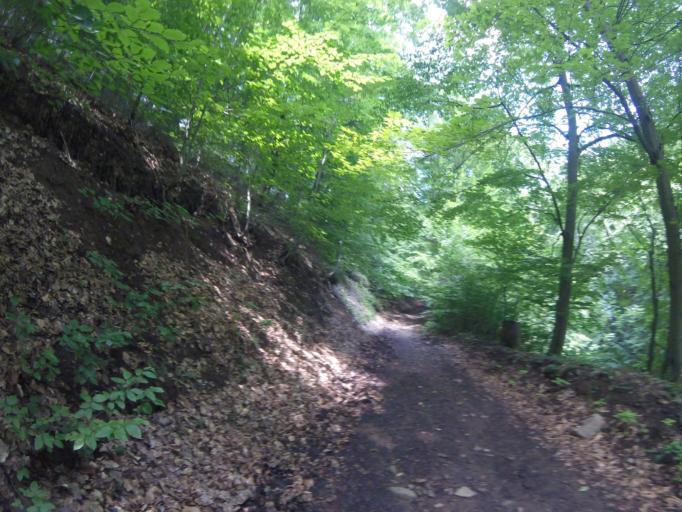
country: SK
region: Nitriansky
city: Sahy
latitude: 47.9604
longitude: 18.8965
